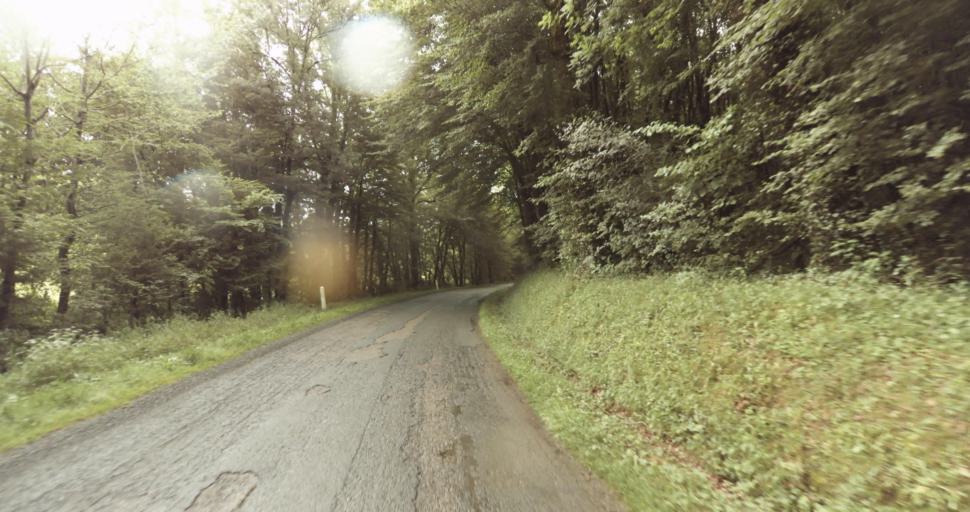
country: FR
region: Aquitaine
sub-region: Departement de la Dordogne
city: Belves
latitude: 44.7541
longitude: 0.9399
